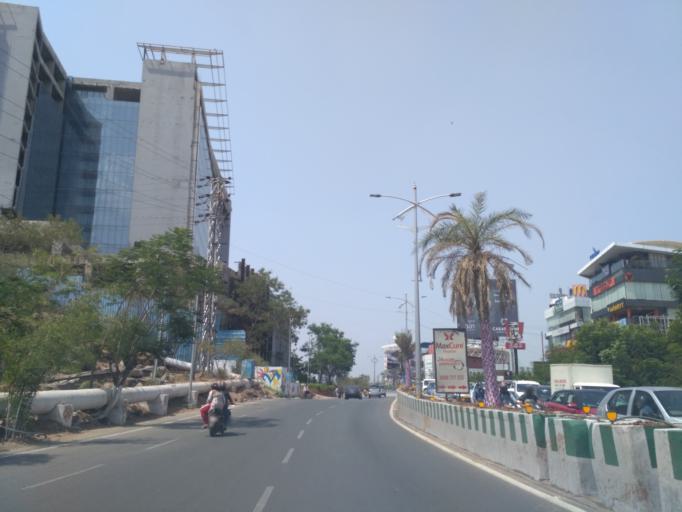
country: IN
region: Telangana
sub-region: Rangareddi
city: Kukatpalli
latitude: 17.4474
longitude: 78.3781
